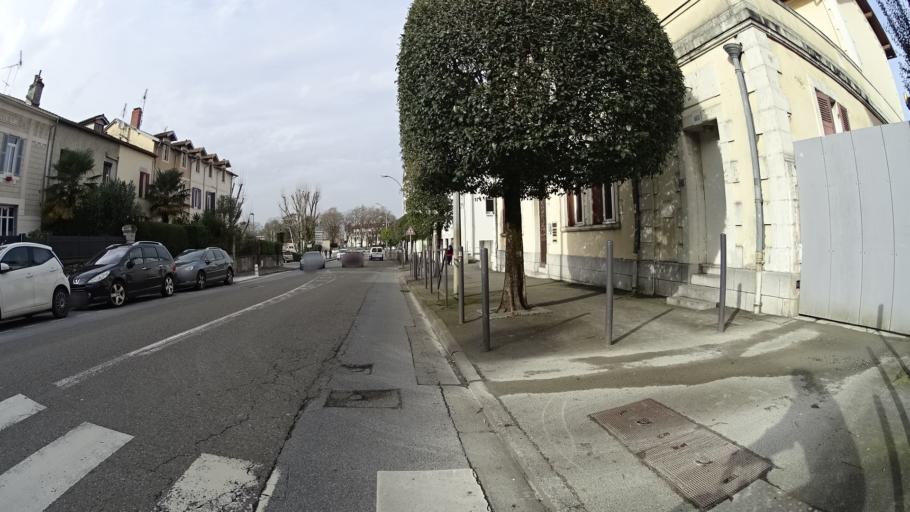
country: FR
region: Aquitaine
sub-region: Departement des Landes
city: Dax
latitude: 43.7101
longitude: -1.0497
